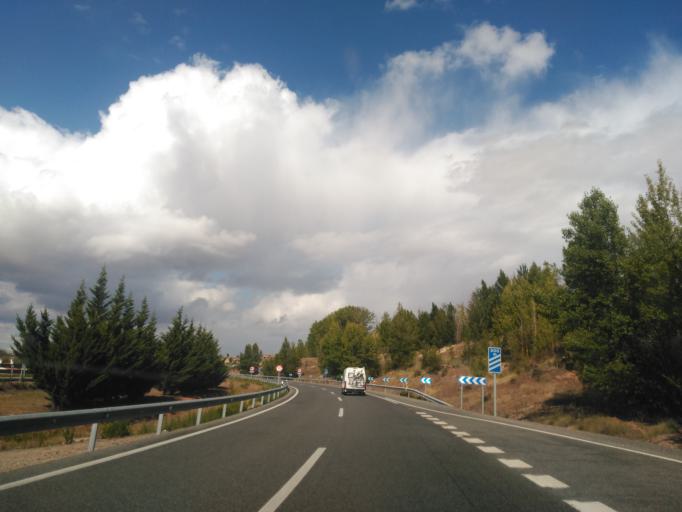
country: ES
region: Castille and Leon
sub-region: Provincia de Burgos
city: Buniel
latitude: 42.3046
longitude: -3.8241
